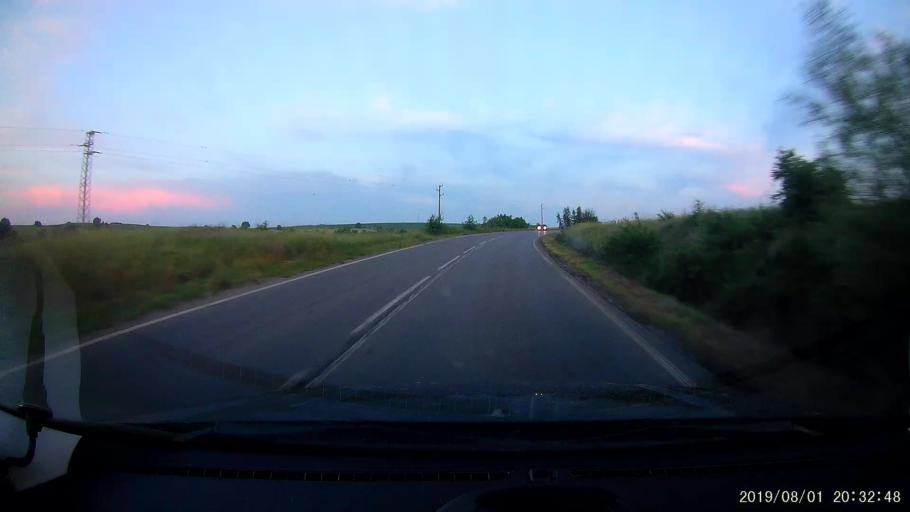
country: BG
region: Yambol
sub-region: Obshtina Elkhovo
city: Elkhovo
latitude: 42.1165
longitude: 26.5310
